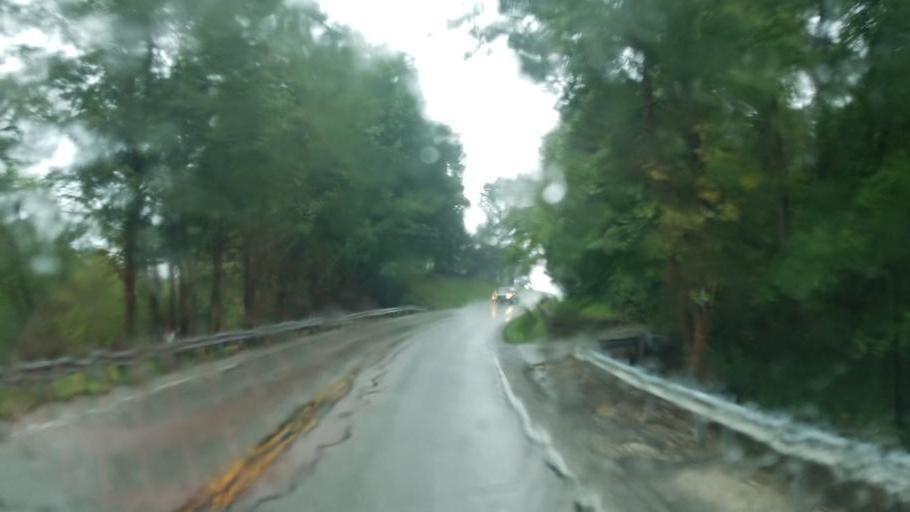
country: US
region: Kentucky
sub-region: Rowan County
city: Morehead
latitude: 38.1632
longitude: -83.4473
